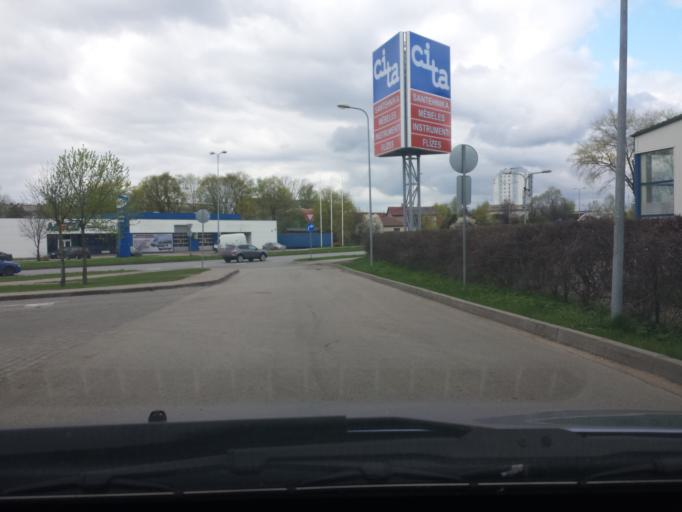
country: LV
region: Riga
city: Riga
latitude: 56.9521
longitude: 24.1879
